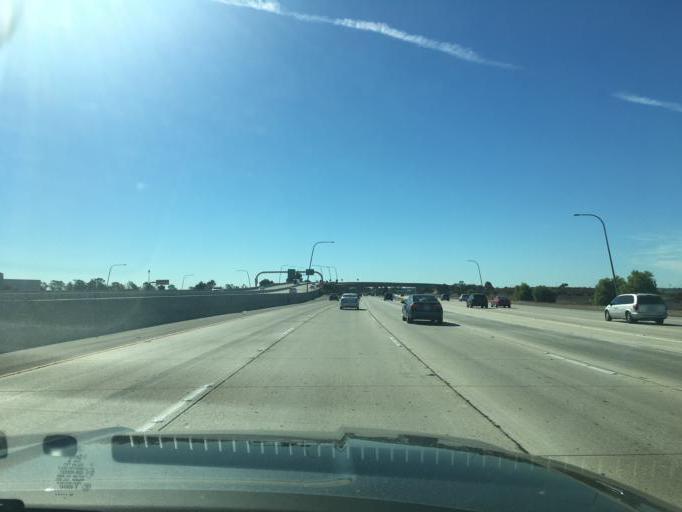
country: US
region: California
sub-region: San Diego County
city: Poway
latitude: 32.8661
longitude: -117.1093
